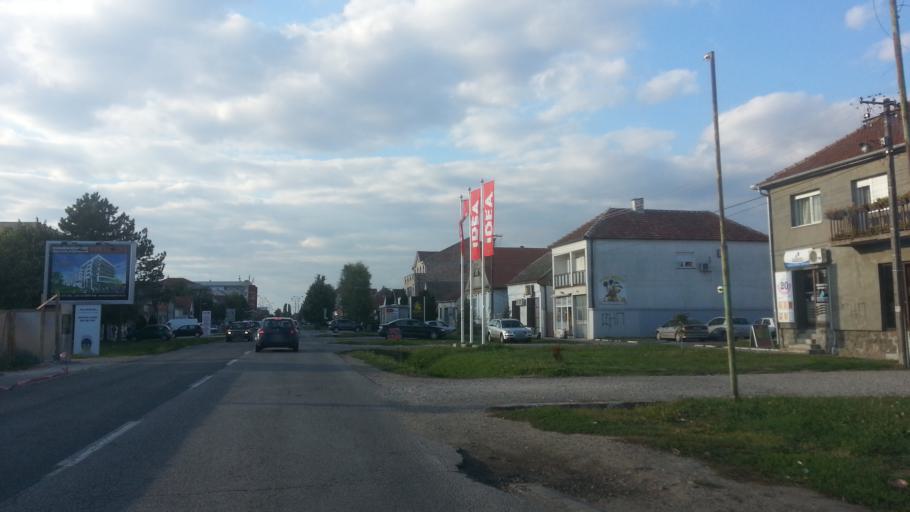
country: RS
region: Autonomna Pokrajina Vojvodina
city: Nova Pazova
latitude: 44.9422
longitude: 20.2224
